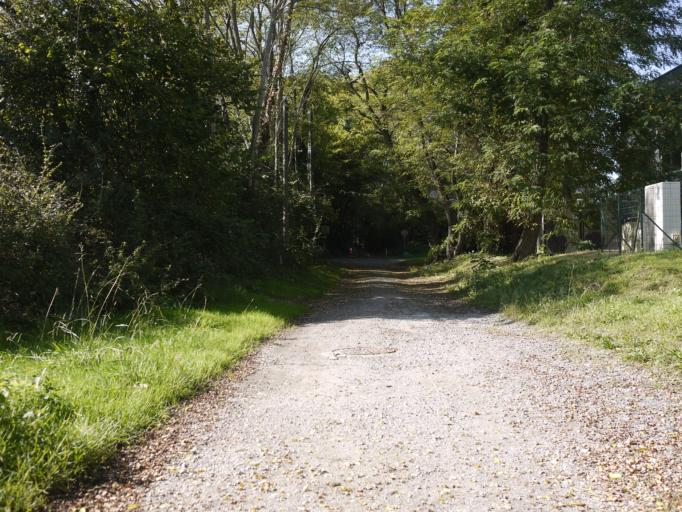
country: FR
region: Aquitaine
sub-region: Departement des Landes
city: Saint-Paul-les-Dax
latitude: 43.7242
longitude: -1.0718
